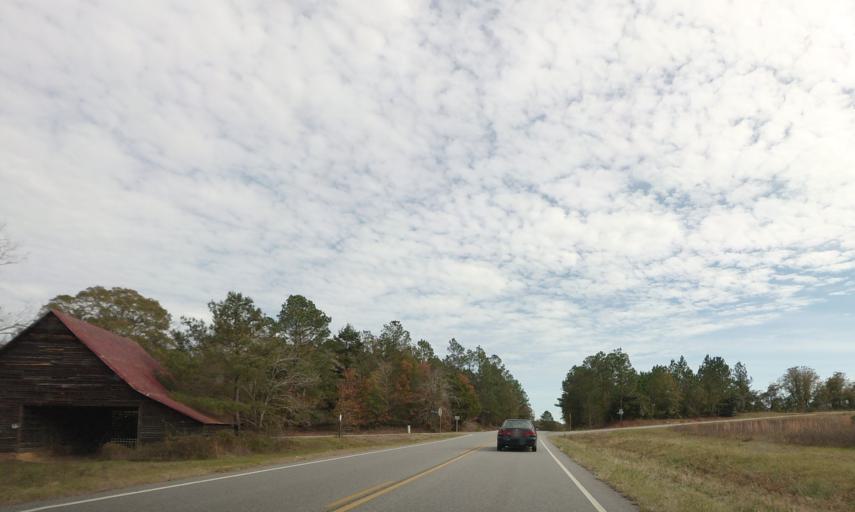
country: US
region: Georgia
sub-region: Dodge County
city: Chester
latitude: 32.4103
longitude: -83.2471
